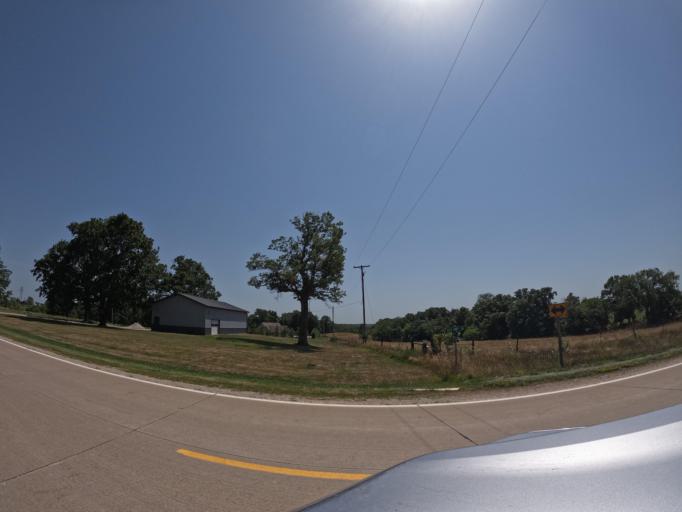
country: US
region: Iowa
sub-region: Henry County
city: Mount Pleasant
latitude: 40.9858
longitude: -91.6362
